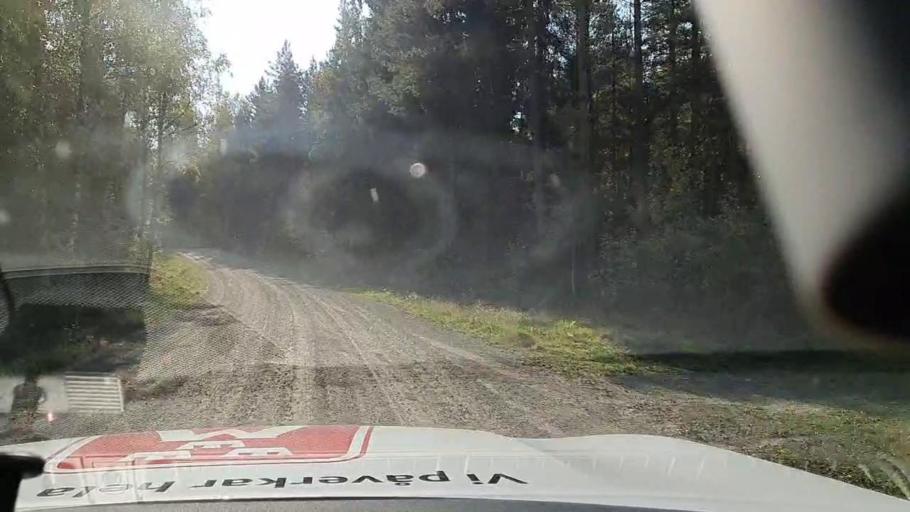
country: SE
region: Soedermanland
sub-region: Eskilstuna Kommun
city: Kvicksund
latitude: 59.3257
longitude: 16.2354
